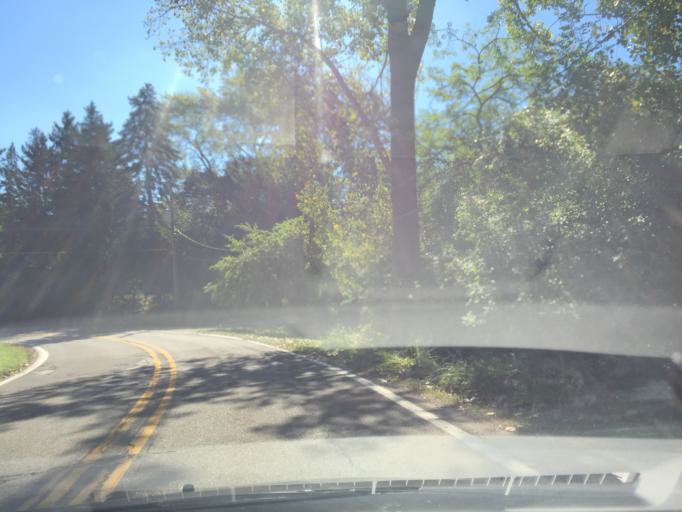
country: US
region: Michigan
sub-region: Oakland County
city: Sylvan Lake
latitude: 42.5918
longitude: -83.2925
